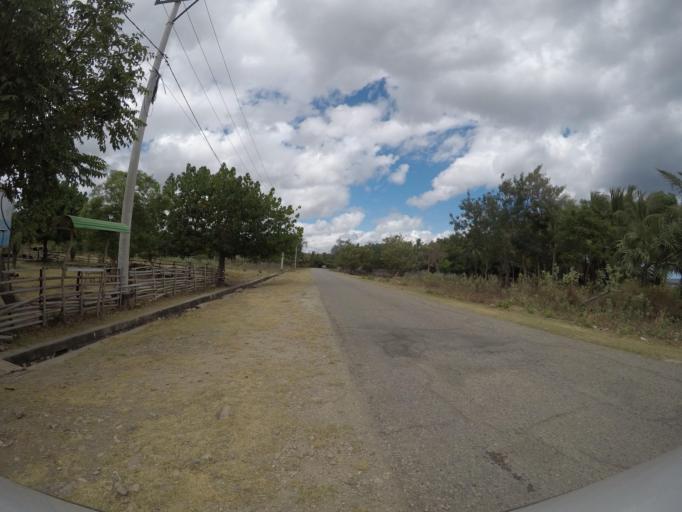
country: TL
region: Lautem
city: Lospalos
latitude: -8.3615
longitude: 126.9055
